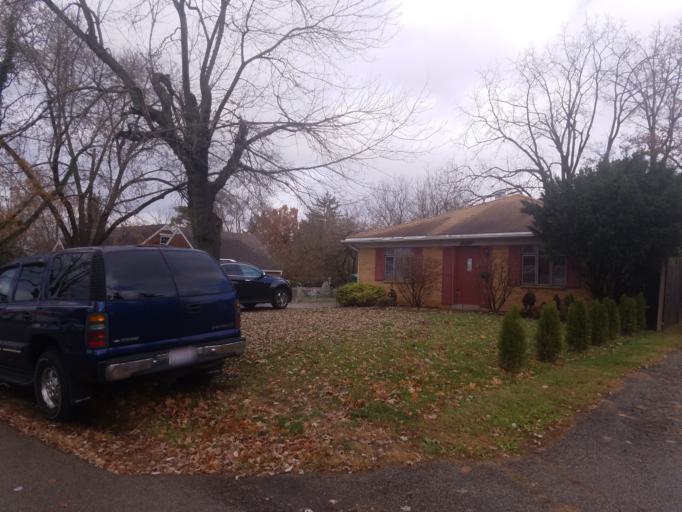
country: US
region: Ohio
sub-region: Montgomery County
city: Kettering
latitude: 39.7091
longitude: -84.1564
